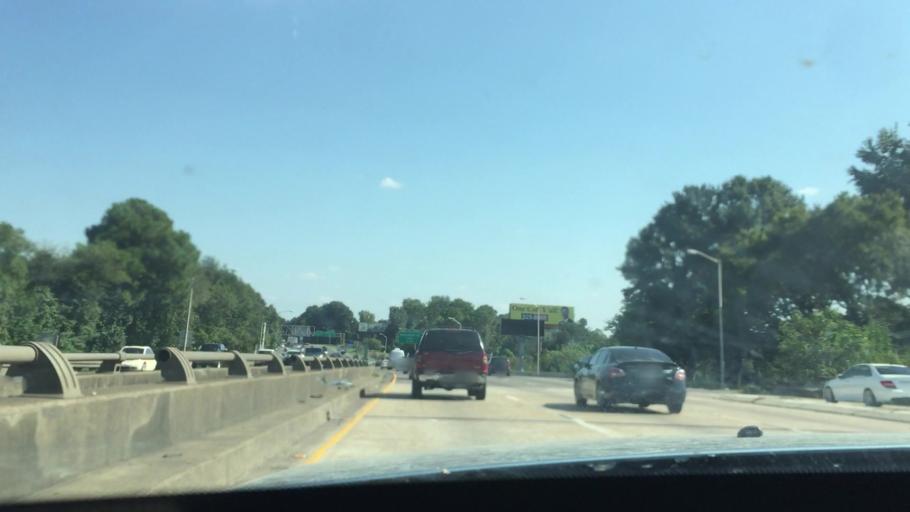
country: US
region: Louisiana
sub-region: East Baton Rouge Parish
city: Baton Rouge
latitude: 30.4309
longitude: -91.1742
